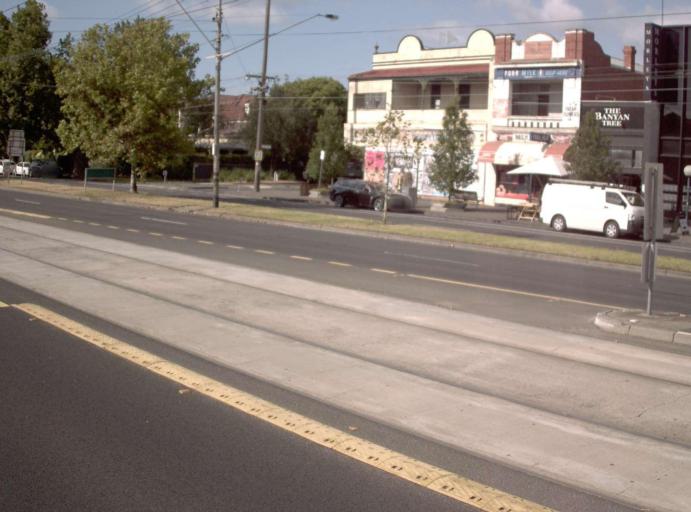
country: AU
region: Victoria
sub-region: Port Phillip
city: Balaclava
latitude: -37.8730
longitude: 144.9903
